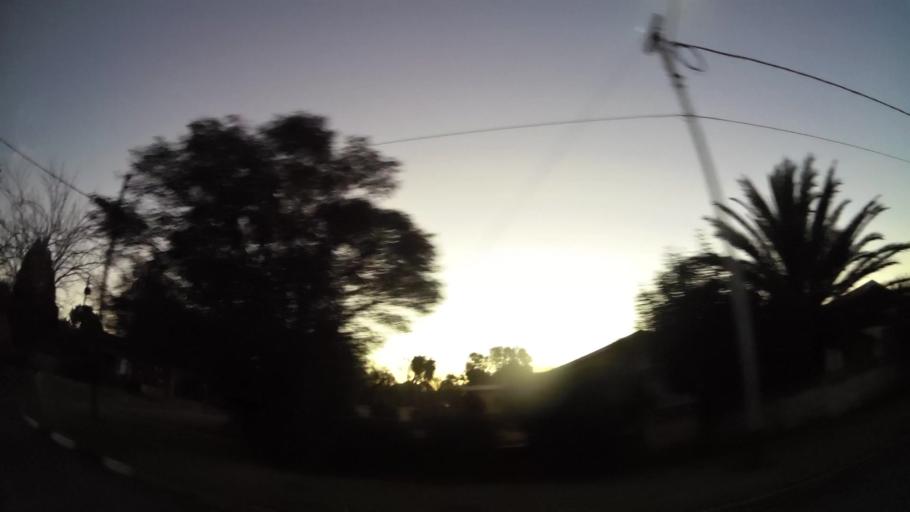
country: ZA
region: Gauteng
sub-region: City of Johannesburg Metropolitan Municipality
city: Roodepoort
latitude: -26.1854
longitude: 27.9256
